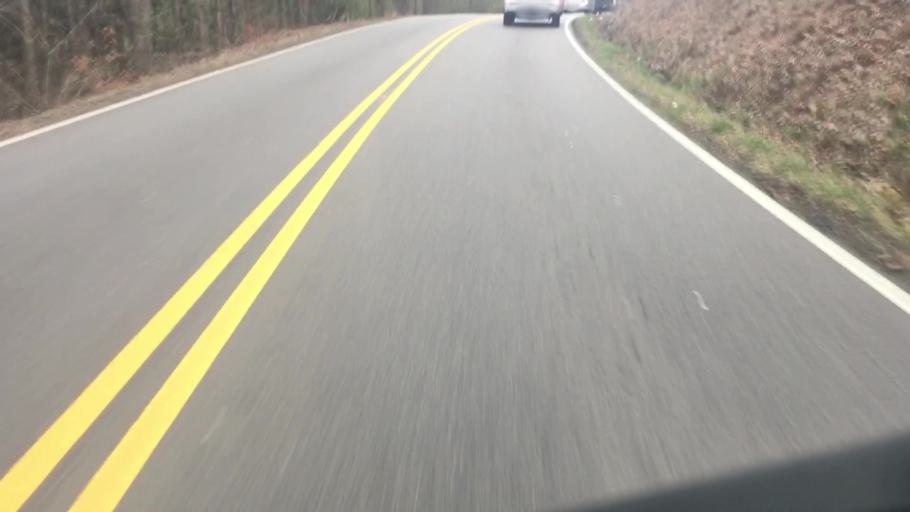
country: US
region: Alabama
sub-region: Jefferson County
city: Cahaba Heights
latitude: 33.4604
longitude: -86.7590
